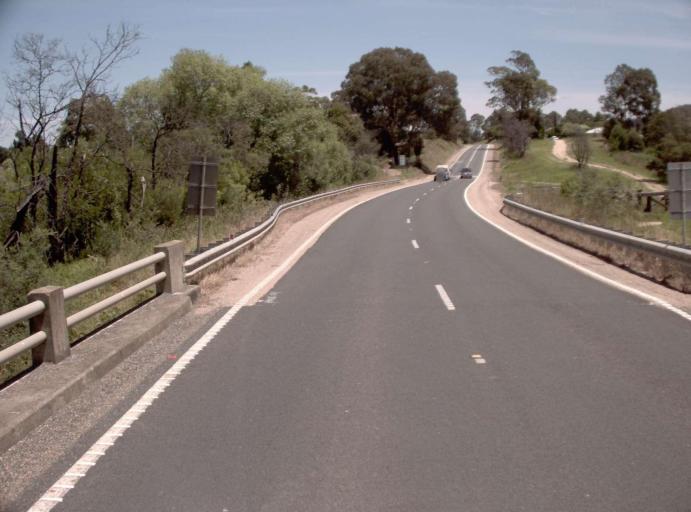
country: AU
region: Victoria
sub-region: East Gippsland
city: Bairnsdale
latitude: -37.7109
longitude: 147.8126
